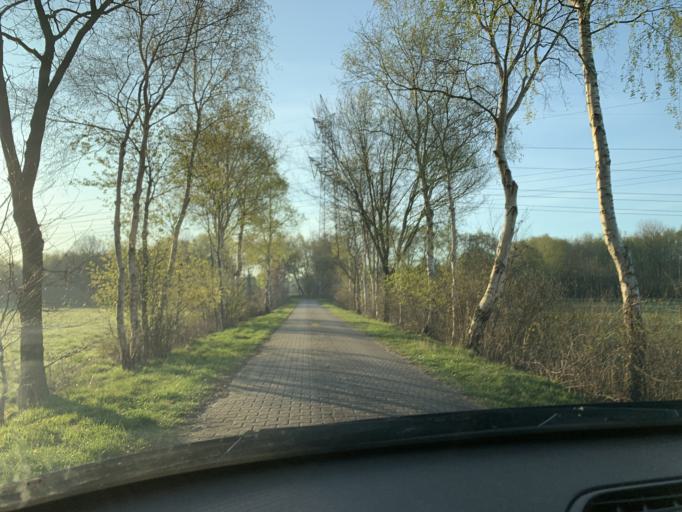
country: DE
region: Lower Saxony
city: Apen
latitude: 53.2865
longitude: 7.8258
